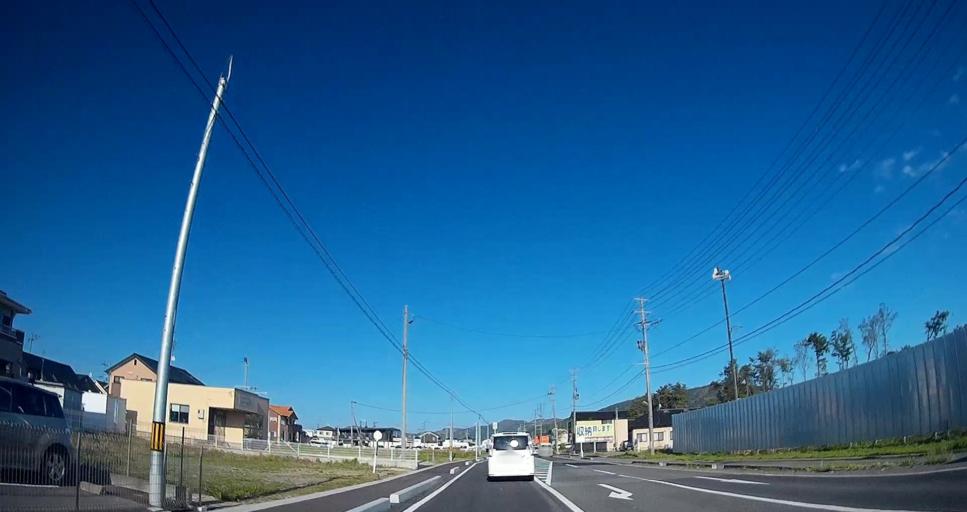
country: JP
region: Miyagi
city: Ishinomaki
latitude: 38.4169
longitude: 141.3528
